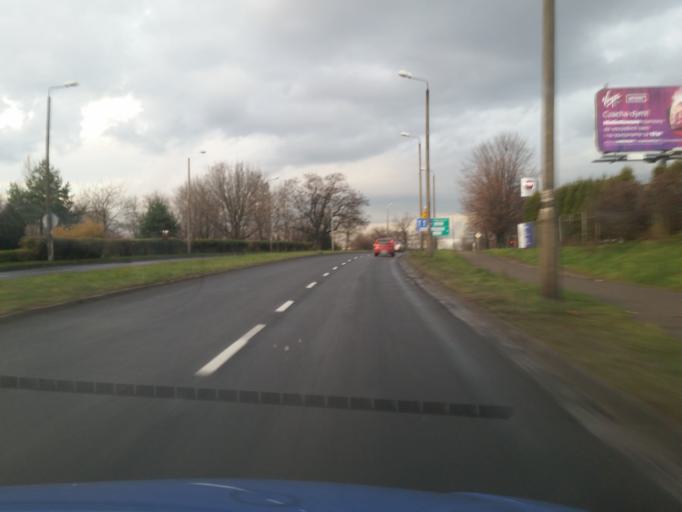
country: PL
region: Silesian Voivodeship
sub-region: Powiat bedzinski
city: Bedzin
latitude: 50.2773
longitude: 19.1749
